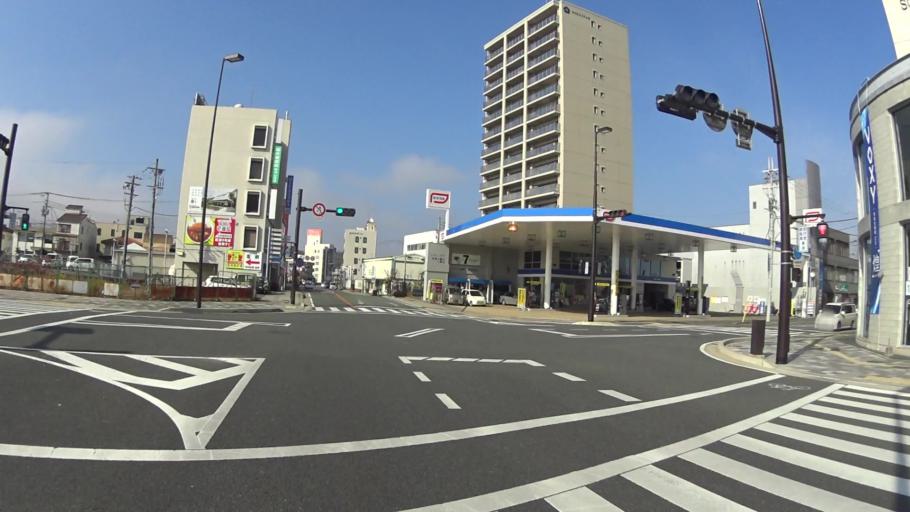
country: JP
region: Kyoto
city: Fukuchiyama
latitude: 35.2981
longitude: 135.1161
